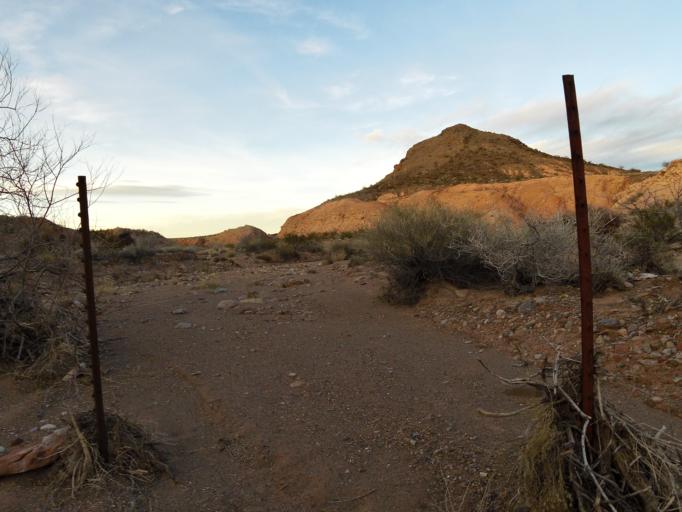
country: US
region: Nevada
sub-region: Clark County
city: Boulder City
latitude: 36.2397
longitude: -114.6332
